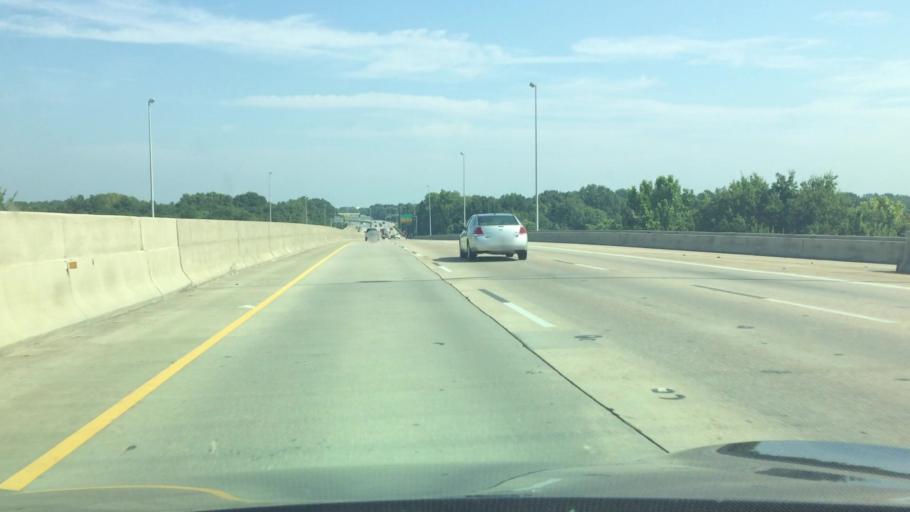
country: US
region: Alabama
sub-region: Montgomery County
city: Montgomery
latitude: 32.3777
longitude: -86.3219
